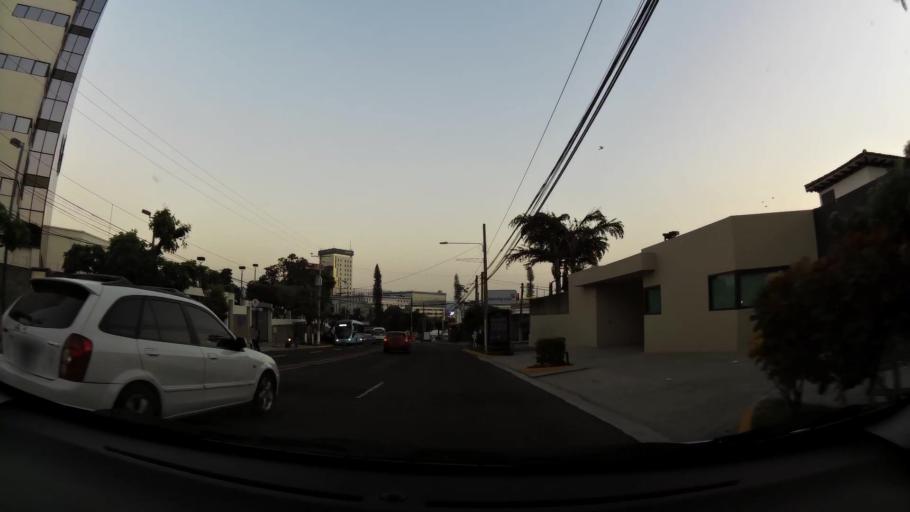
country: SV
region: San Salvador
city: Mejicanos
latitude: 13.7030
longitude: -89.2255
